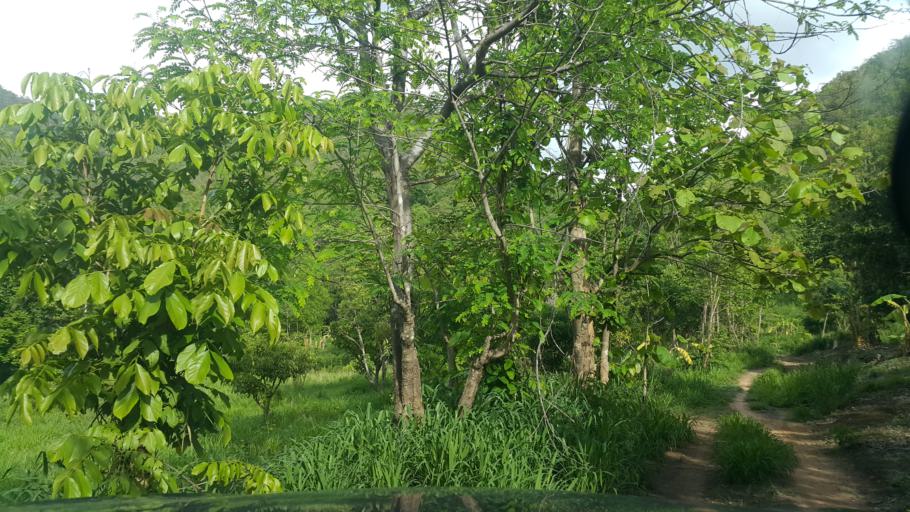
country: TH
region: Chiang Mai
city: Mae On
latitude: 18.7083
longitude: 99.2161
